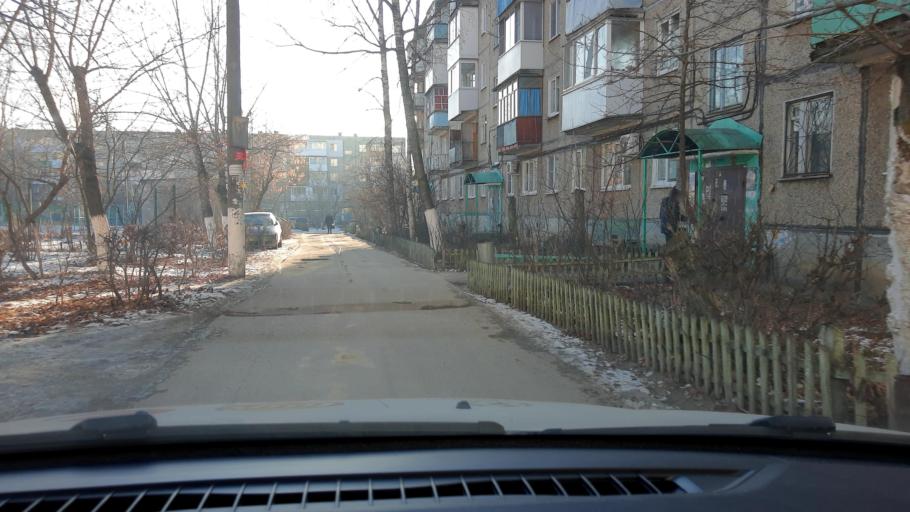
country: RU
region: Nizjnij Novgorod
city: Dzerzhinsk
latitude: 56.2321
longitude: 43.4190
